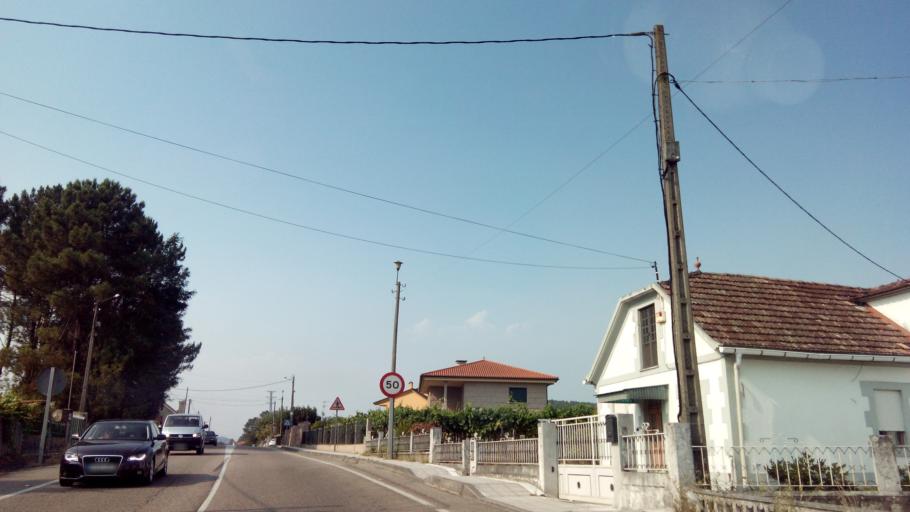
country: ES
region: Galicia
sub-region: Provincia de Pontevedra
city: Ponteareas
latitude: 42.1850
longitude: -8.5069
